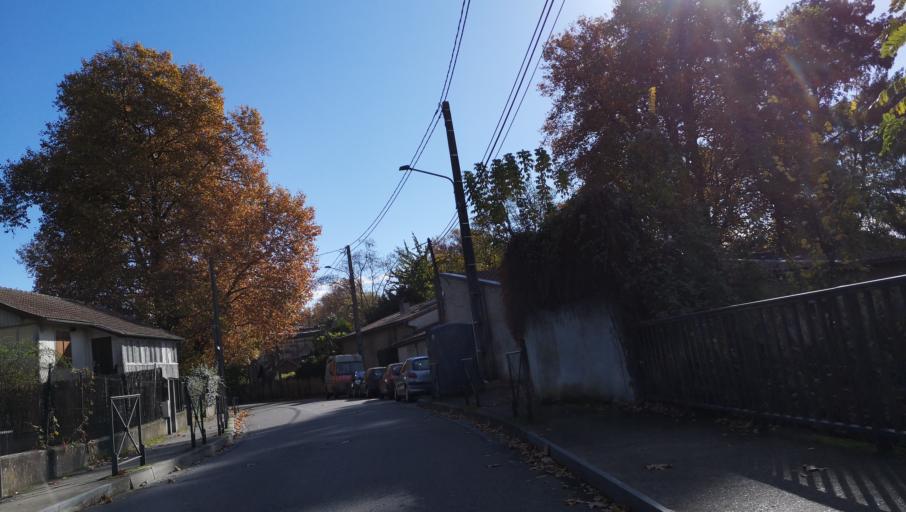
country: FR
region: Midi-Pyrenees
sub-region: Departement de la Haute-Garonne
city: Toulouse
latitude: 43.6088
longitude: 1.4159
